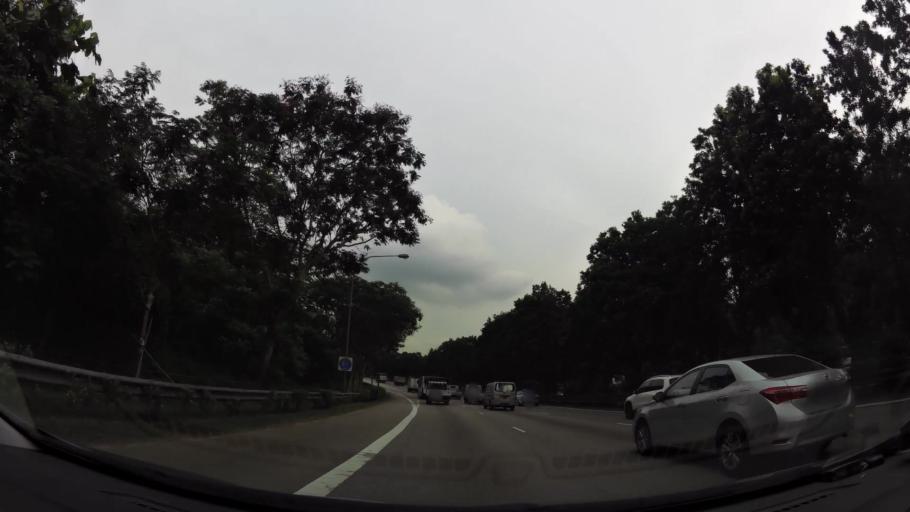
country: MY
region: Johor
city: Johor Bahru
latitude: 1.3960
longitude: 103.8152
